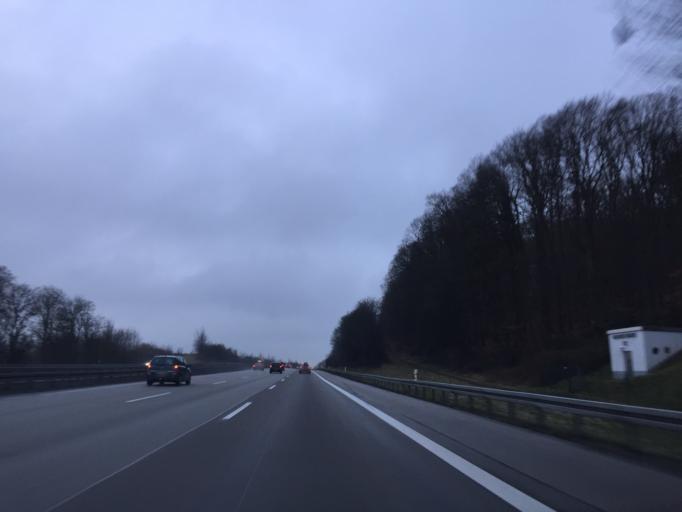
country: DE
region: Hesse
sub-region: Regierungsbezirk Darmstadt
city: Idstein
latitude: 50.2345
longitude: 8.2468
